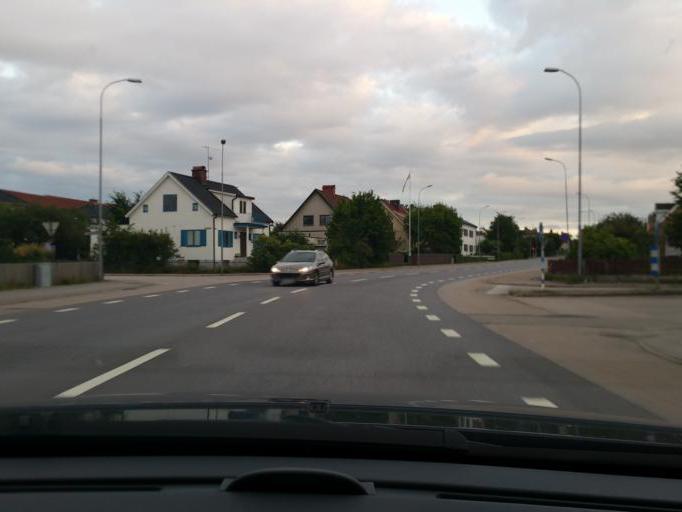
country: SE
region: Kronoberg
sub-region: Alvesta Kommun
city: Alvesta
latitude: 56.9048
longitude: 14.5569
